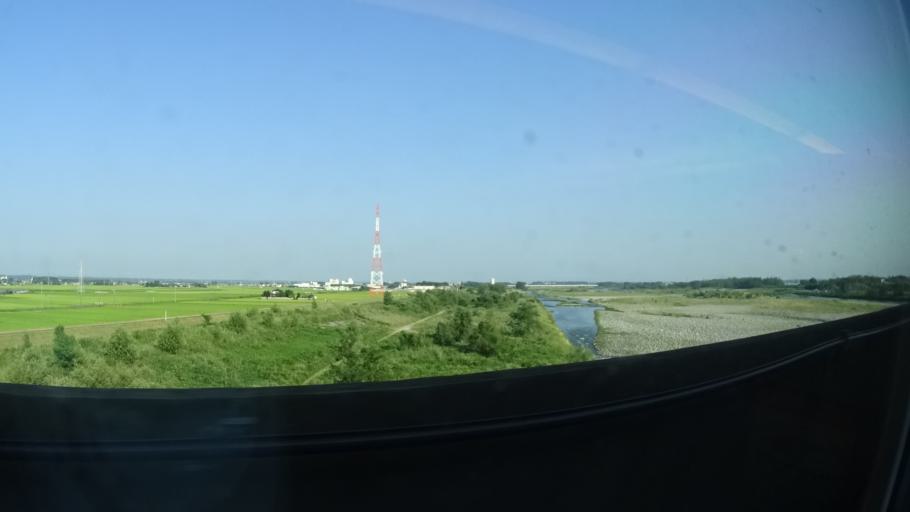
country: JP
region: Tochigi
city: Ujiie
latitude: 36.7102
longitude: 139.9228
